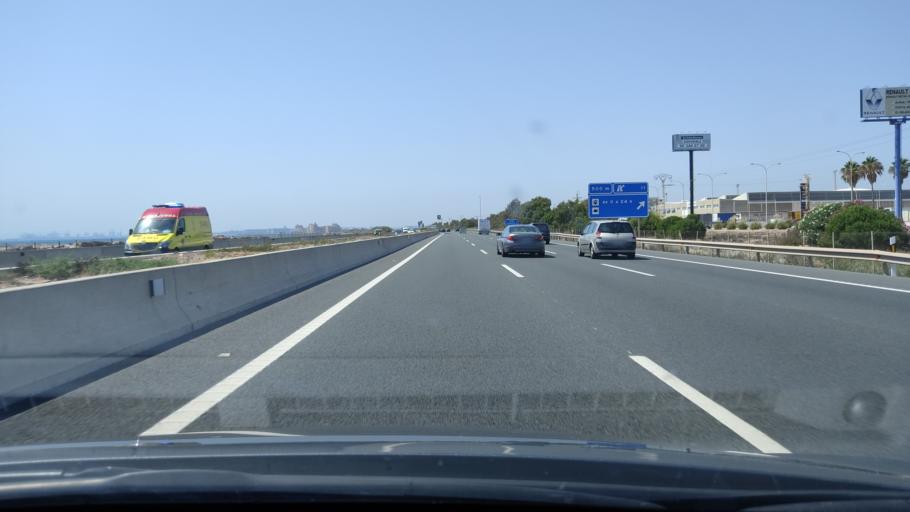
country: ES
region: Valencia
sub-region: Provincia de Valencia
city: Albuixech
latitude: 39.5375
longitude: -0.3067
